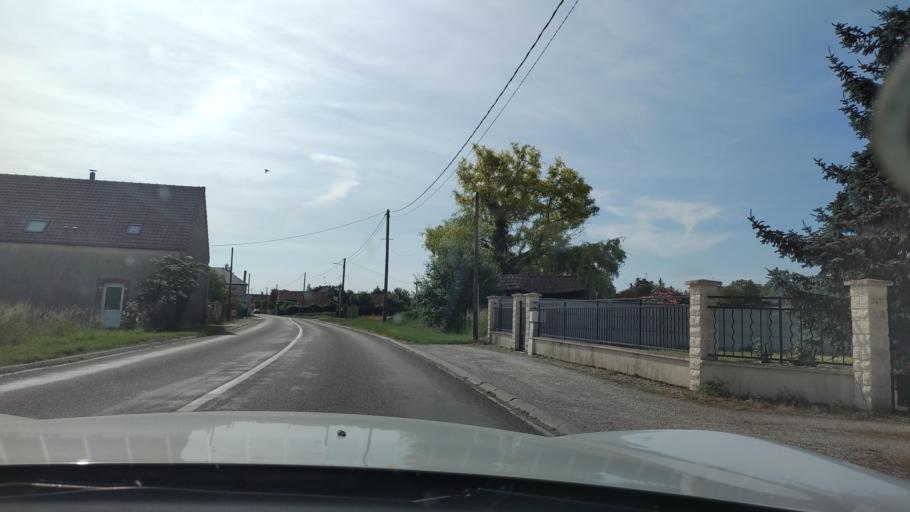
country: FR
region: Champagne-Ardenne
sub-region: Departement de l'Aube
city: Marigny-le-Chatel
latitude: 48.4417
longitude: 3.6486
